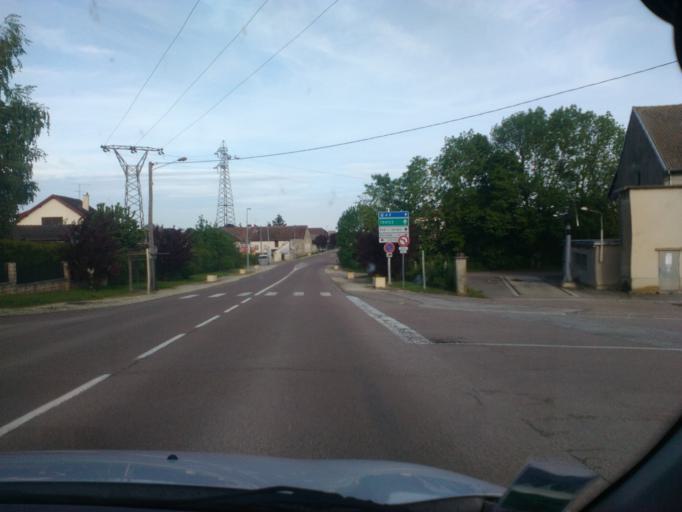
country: FR
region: Champagne-Ardenne
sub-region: Departement de l'Aube
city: Vendeuvre-sur-Barse
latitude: 48.2395
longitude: 4.4765
